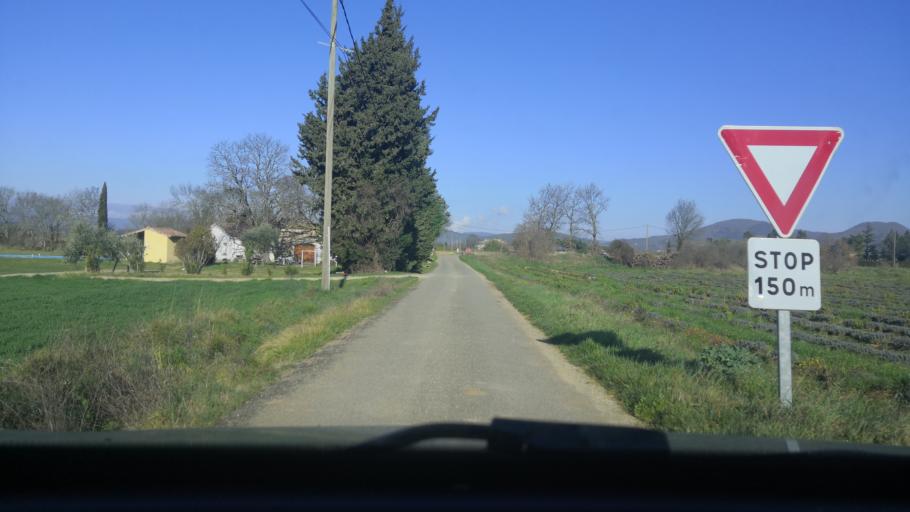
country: FR
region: Rhone-Alpes
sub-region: Departement de la Drome
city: Sauzet
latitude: 44.5736
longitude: 4.8363
